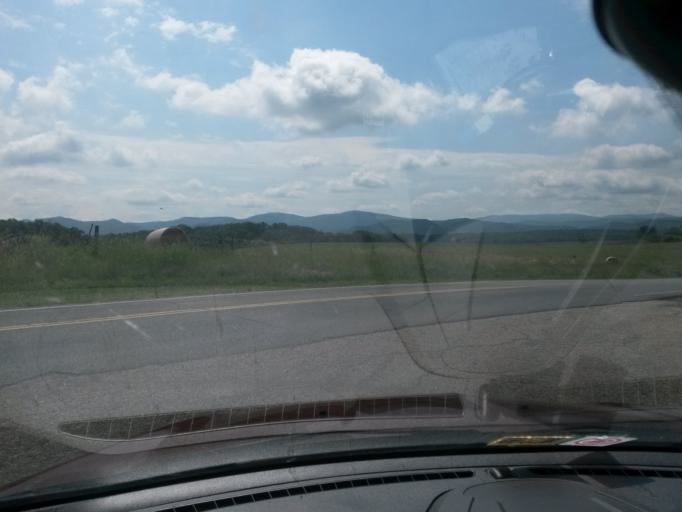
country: US
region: Virginia
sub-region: Augusta County
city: Stuarts Draft
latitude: 37.9268
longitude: -79.2273
